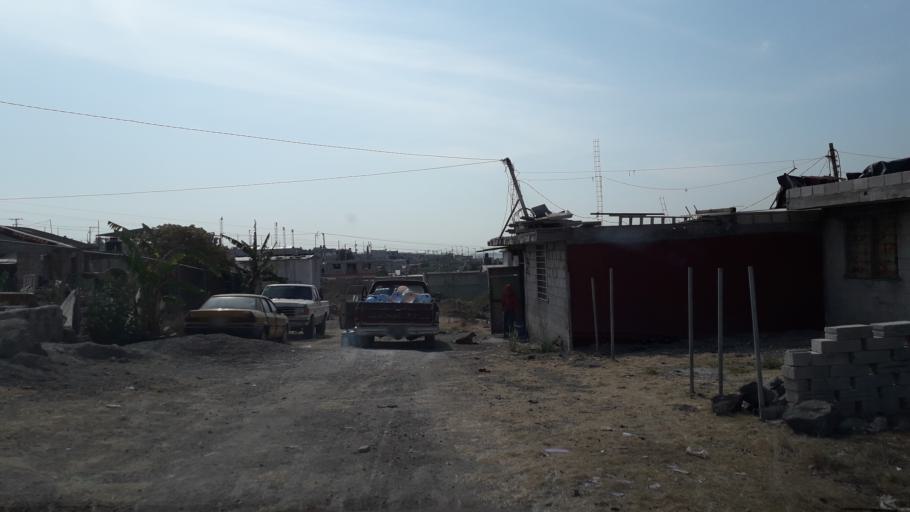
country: MX
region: Puebla
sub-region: Puebla
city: El Capulo (La Quebradora)
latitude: 18.9349
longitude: -98.2702
